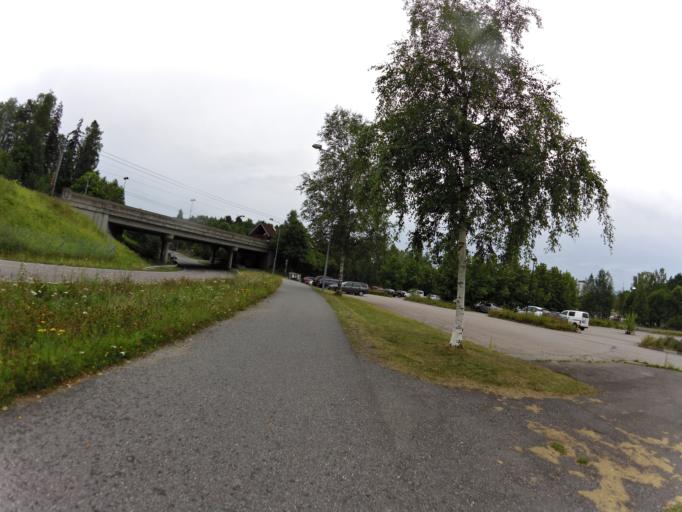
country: NO
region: Ostfold
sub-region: Moss
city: Moss
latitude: 59.4788
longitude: 10.6923
